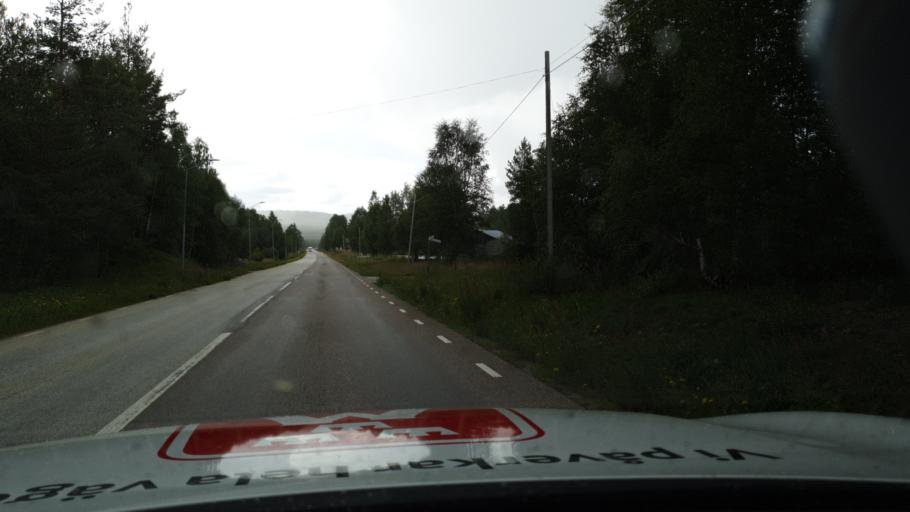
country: SE
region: Jaemtland
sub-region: Harjedalens Kommun
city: Sveg
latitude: 62.4373
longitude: 13.8430
